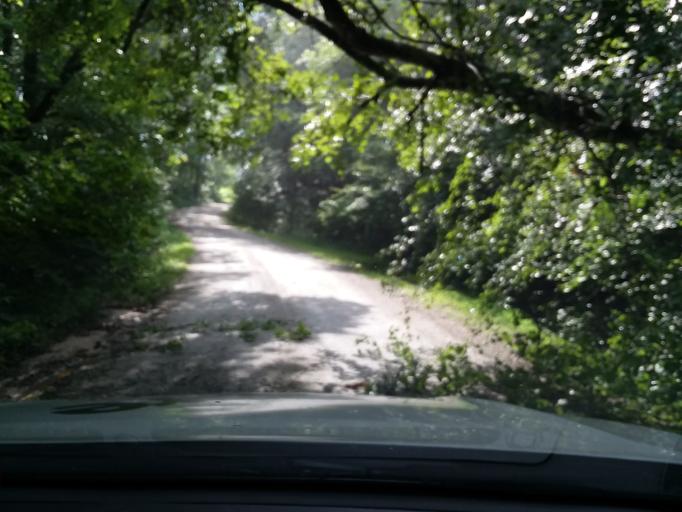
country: US
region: Georgia
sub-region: Habersham County
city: Clarkesville
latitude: 34.7117
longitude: -83.4263
